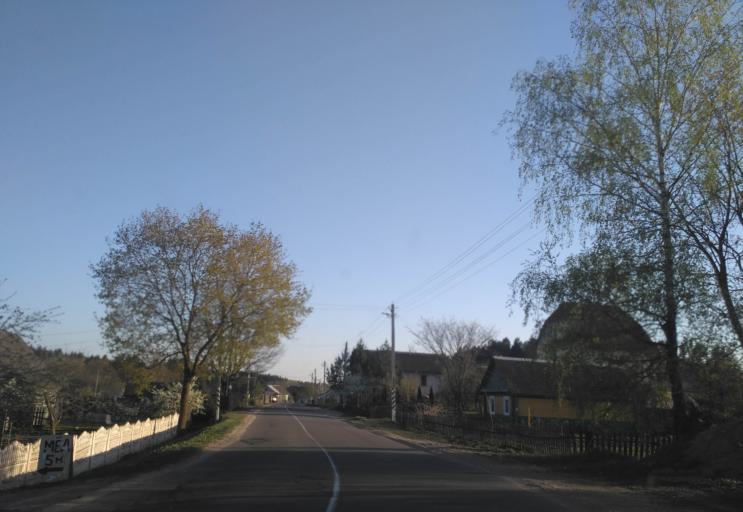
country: BY
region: Minsk
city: Radashkovichy
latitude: 54.1516
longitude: 27.2175
